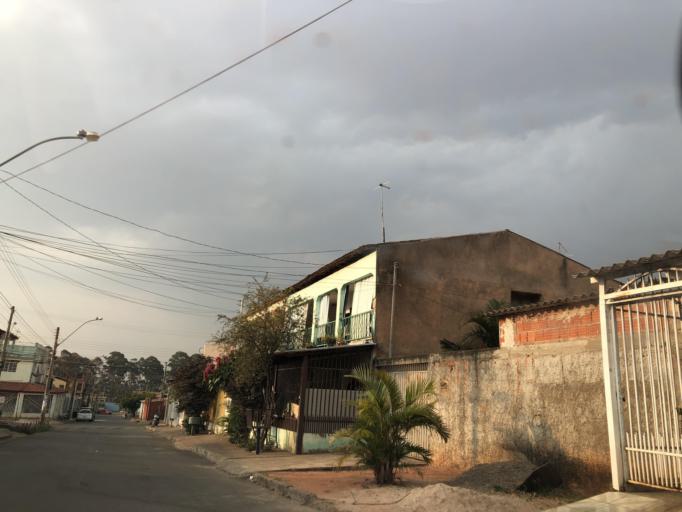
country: BR
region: Federal District
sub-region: Brasilia
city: Brasilia
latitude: -15.9022
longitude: -48.0633
